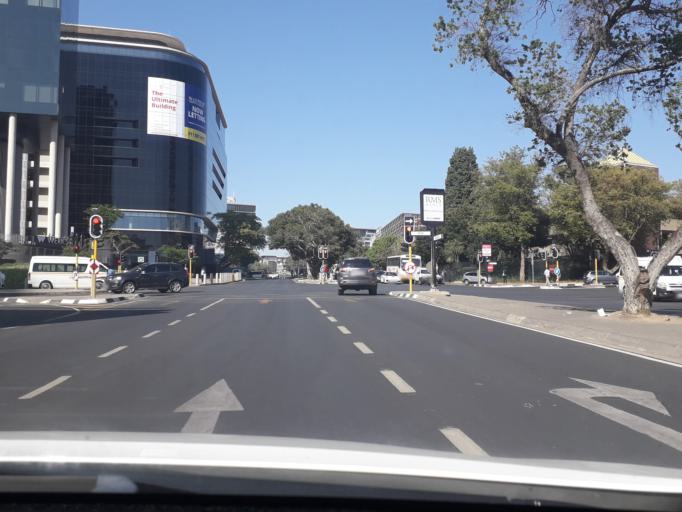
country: ZA
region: Gauteng
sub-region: City of Johannesburg Metropolitan Municipality
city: Johannesburg
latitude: -26.1089
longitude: 28.0566
